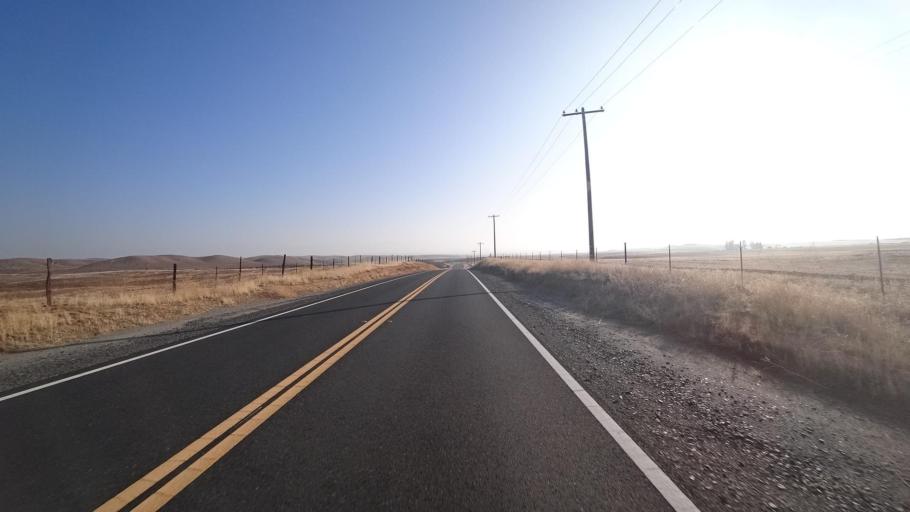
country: US
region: California
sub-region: Tulare County
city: Richgrove
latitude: 35.7620
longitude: -119.0408
